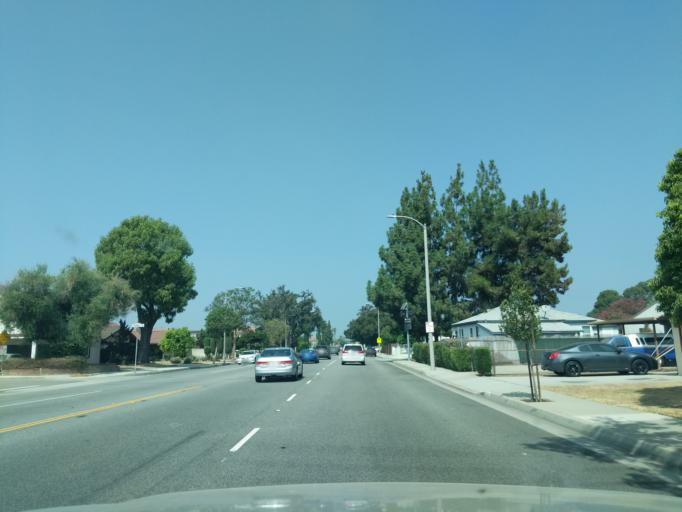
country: US
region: California
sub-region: Los Angeles County
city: East San Gabriel
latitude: 34.0881
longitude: -118.0829
